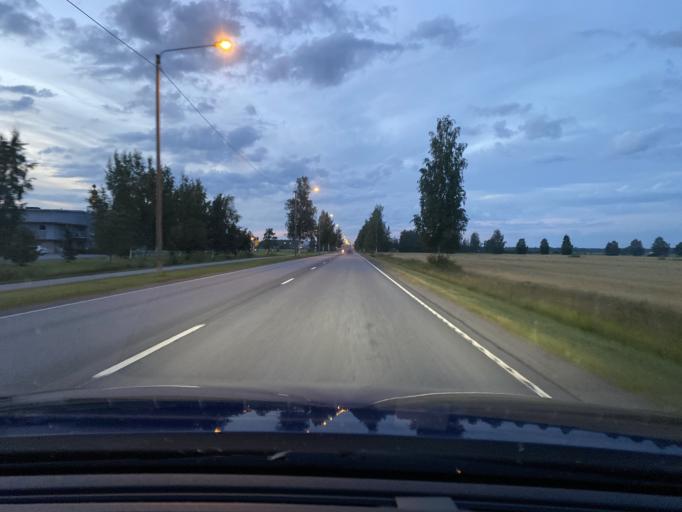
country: FI
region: Southern Ostrobothnia
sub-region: Suupohja
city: Kauhajoki
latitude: 62.4356
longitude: 22.2067
